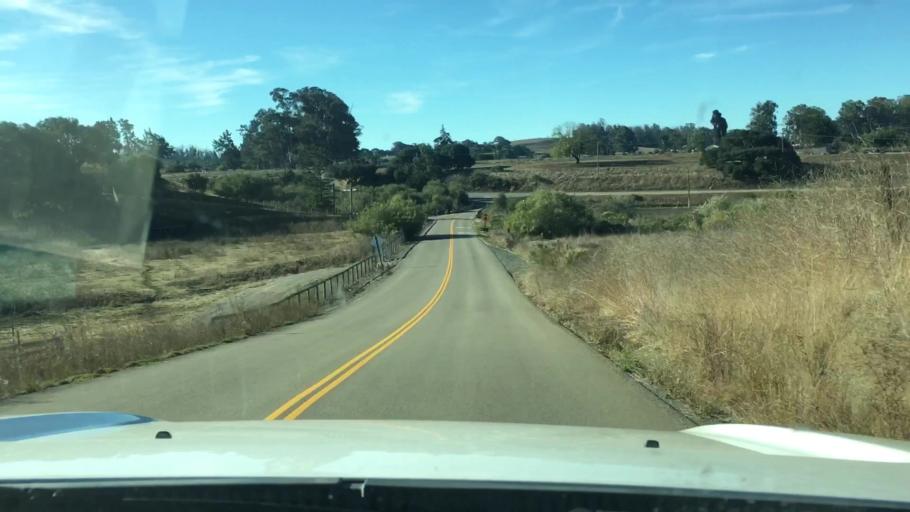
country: US
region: California
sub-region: San Luis Obispo County
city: Arroyo Grande
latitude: 35.0955
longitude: -120.5611
